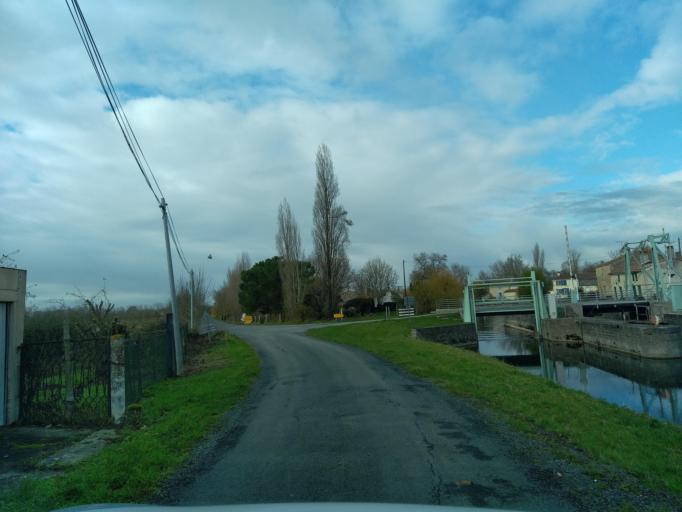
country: FR
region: Pays de la Loire
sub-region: Departement de la Vendee
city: Maillezais
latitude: 46.3175
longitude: -0.7773
